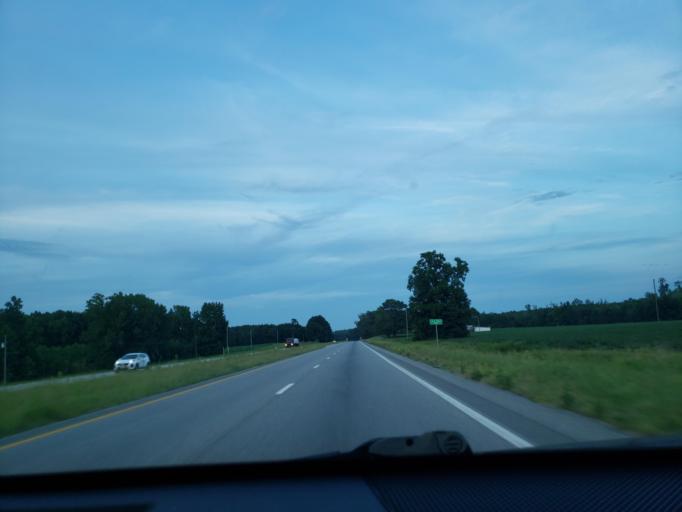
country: US
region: Virginia
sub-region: Southampton County
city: Courtland
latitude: 36.7066
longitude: -77.1778
